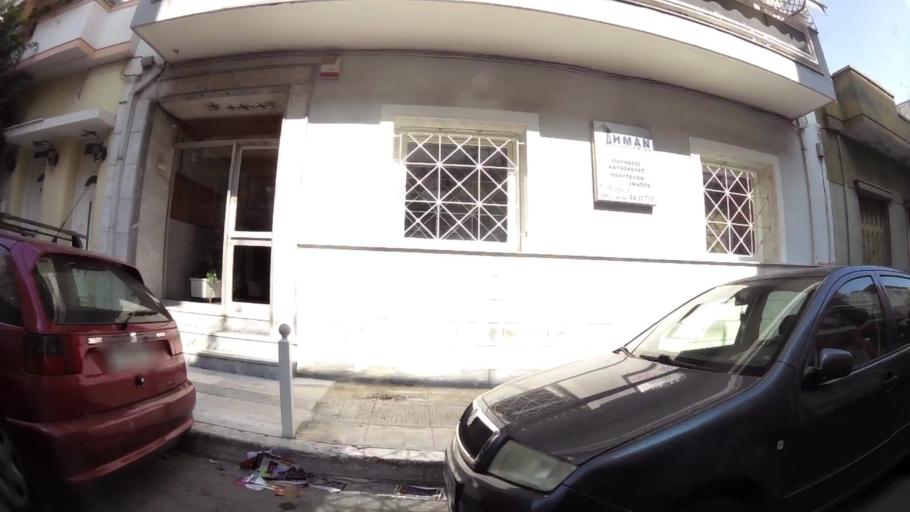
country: GR
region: Attica
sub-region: Nomos Piraios
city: Keratsini
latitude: 37.9585
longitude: 23.6277
